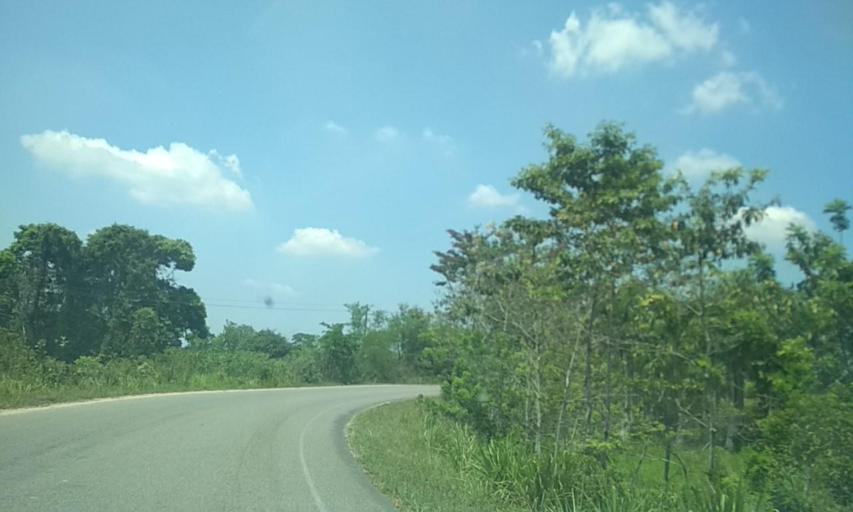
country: MX
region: Tabasco
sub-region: Huimanguillo
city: Paso de la Mina 2da. Seccion (Barrial)
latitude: 17.7803
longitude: -93.6378
